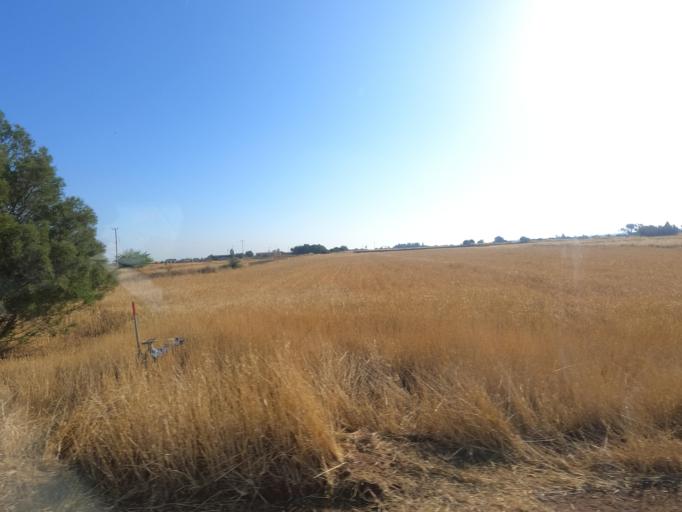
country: CY
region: Ammochostos
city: Frenaros
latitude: 35.0566
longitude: 33.9095
